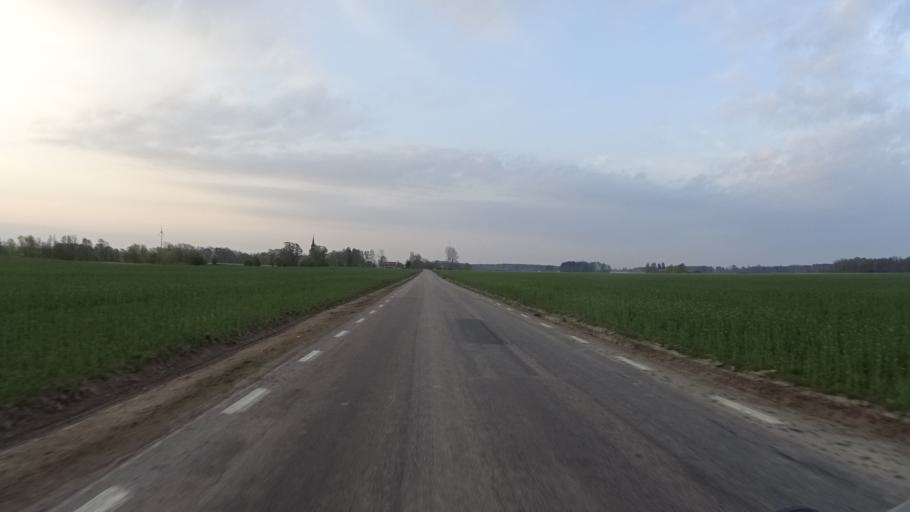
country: SE
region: Vaestra Goetaland
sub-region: Gotene Kommun
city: Kallby
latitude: 58.4781
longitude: 13.3211
